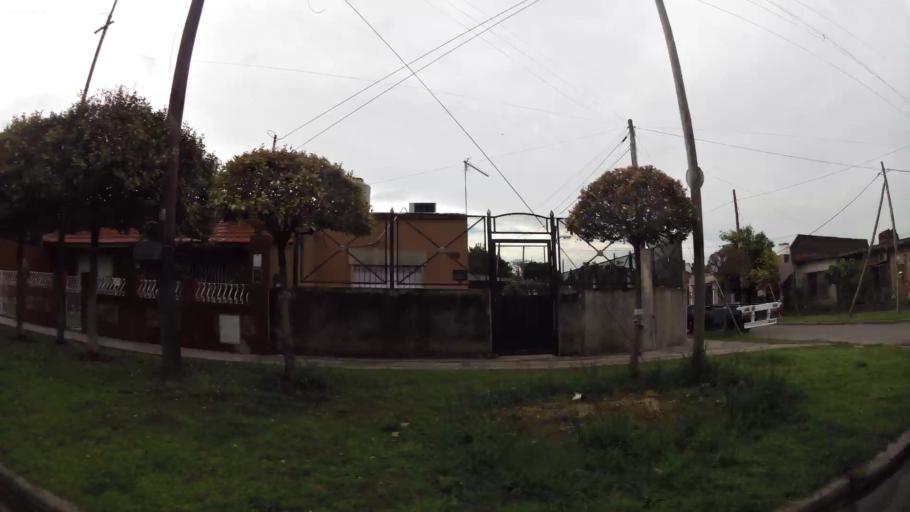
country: AR
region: Buenos Aires
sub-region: Partido de Lomas de Zamora
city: Lomas de Zamora
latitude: -34.7431
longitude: -58.3442
